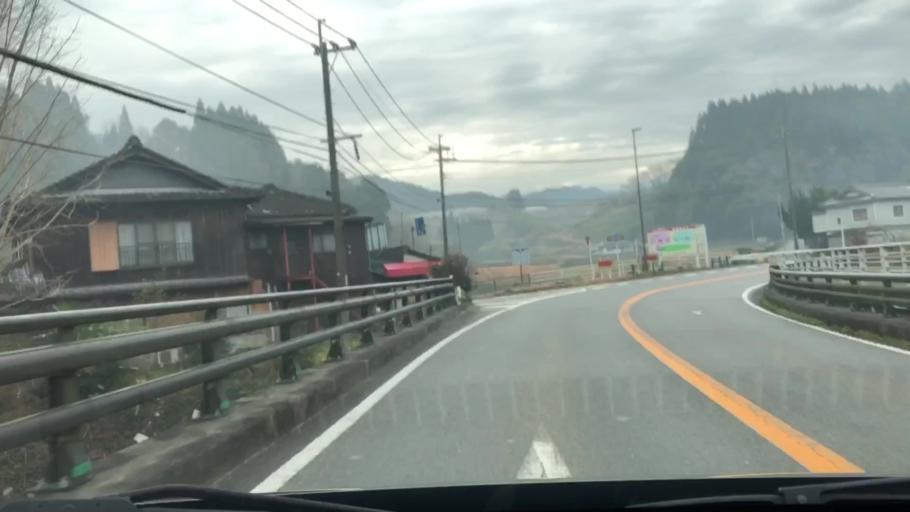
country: JP
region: Oita
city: Usuki
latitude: 33.0175
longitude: 131.7008
